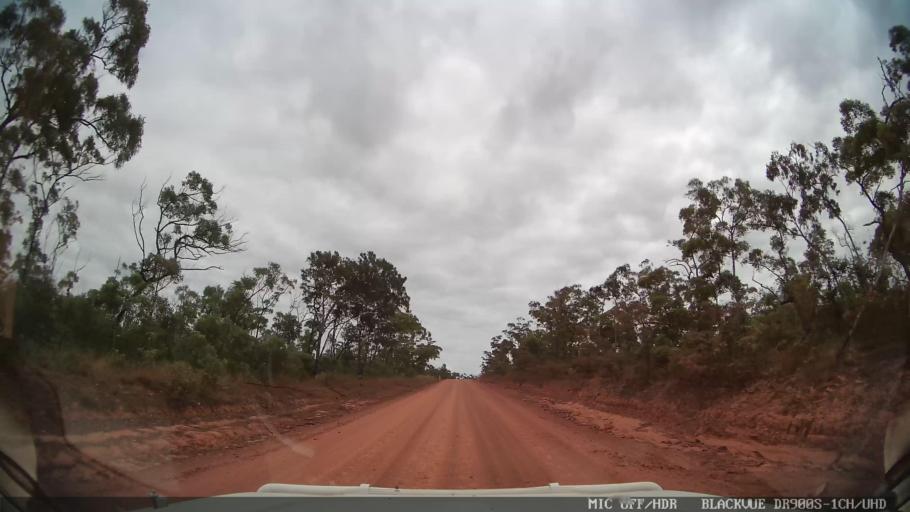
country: AU
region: Queensland
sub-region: Cook
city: Cooktown
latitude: -15.2669
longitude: 144.9462
